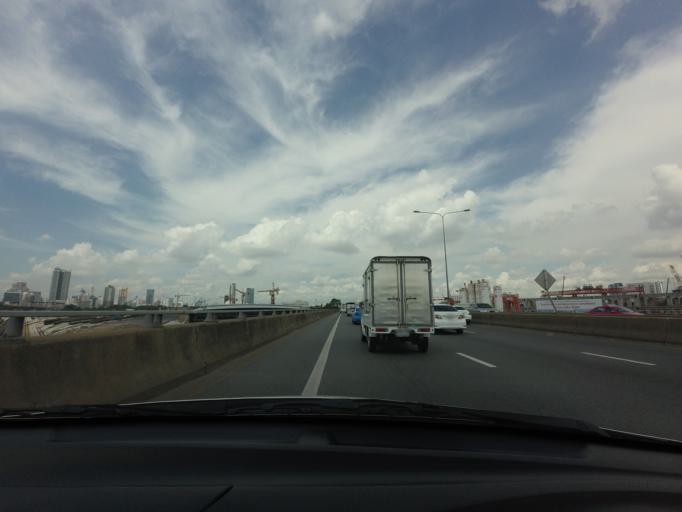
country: TH
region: Bangkok
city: Bang Sue
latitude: 13.8047
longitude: 100.5457
